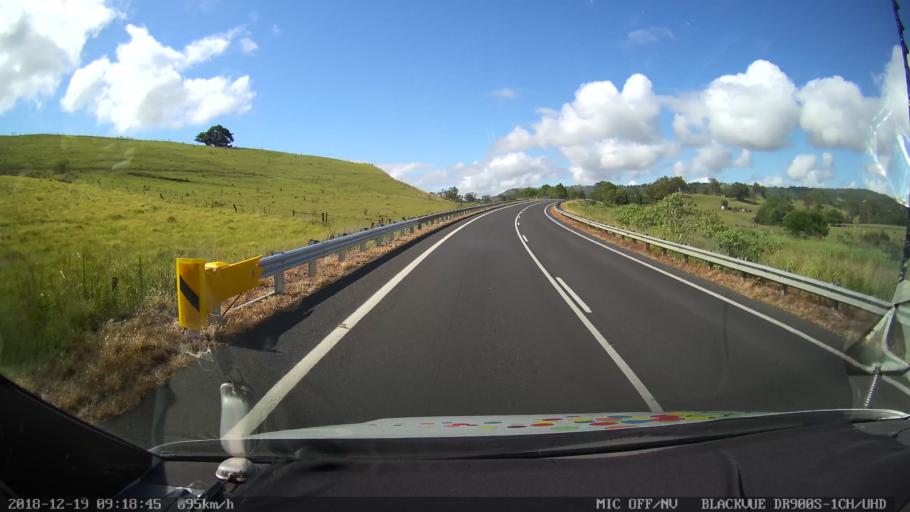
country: AU
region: New South Wales
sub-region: Kyogle
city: Kyogle
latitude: -28.5517
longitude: 152.9765
